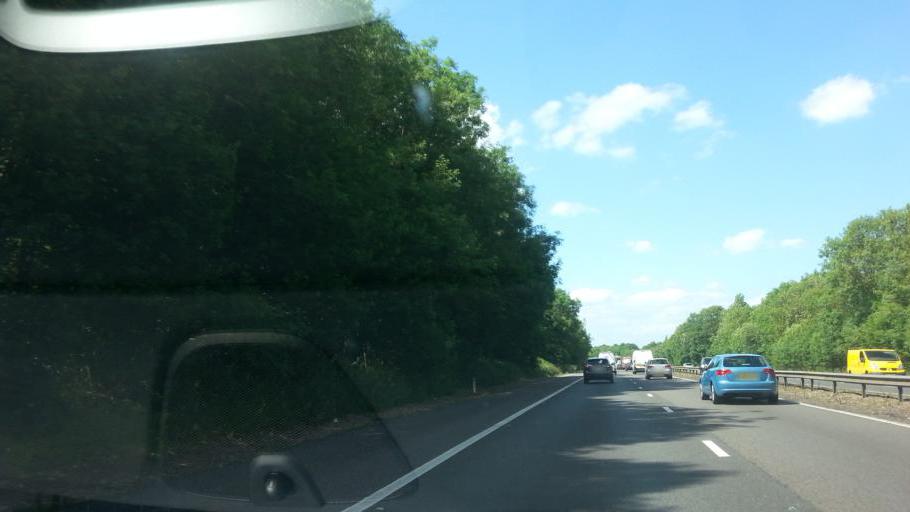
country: GB
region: England
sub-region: Hertfordshire
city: Knebworth
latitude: 51.8589
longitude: -0.1964
